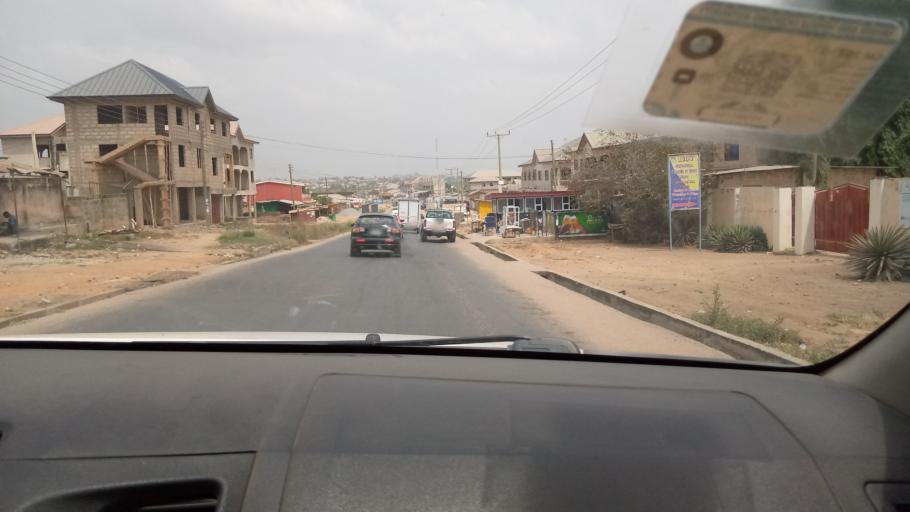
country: GH
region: Central
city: Kasoa
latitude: 5.5321
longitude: -0.4510
